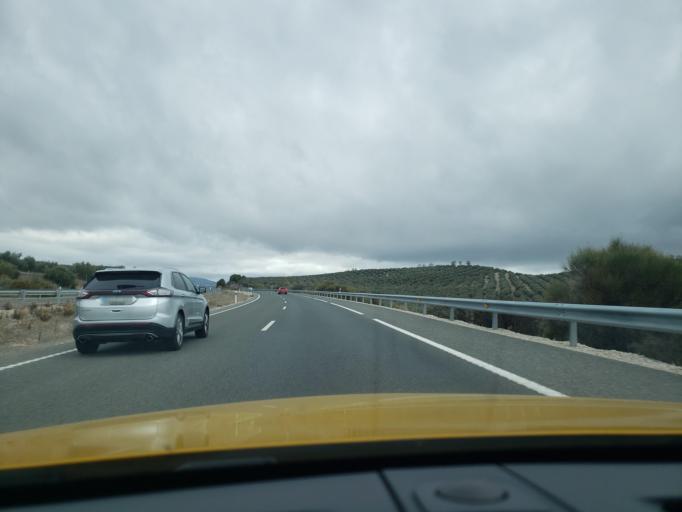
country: ES
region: Andalusia
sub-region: Provincia de Granada
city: Campotejar
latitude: 37.4832
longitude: -3.5720
